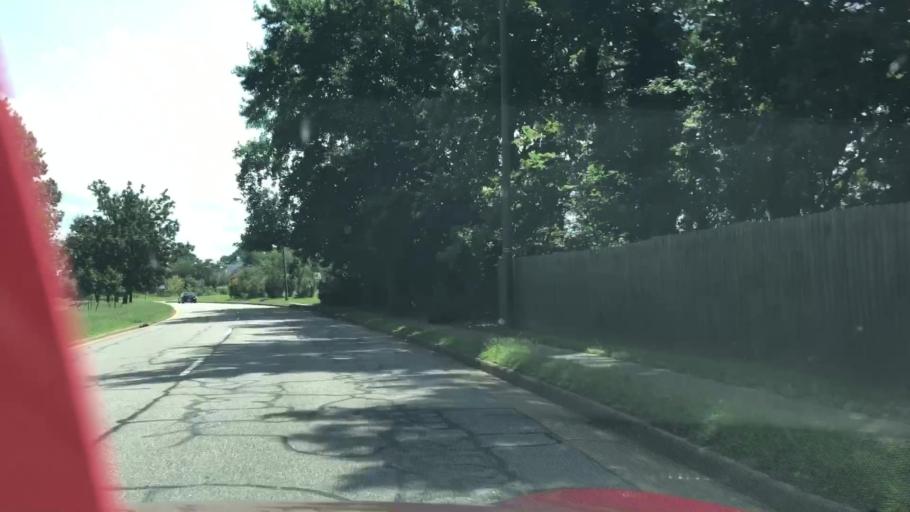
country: US
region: Virginia
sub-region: City of Virginia Beach
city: Virginia Beach
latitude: 36.8702
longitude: -76.0350
